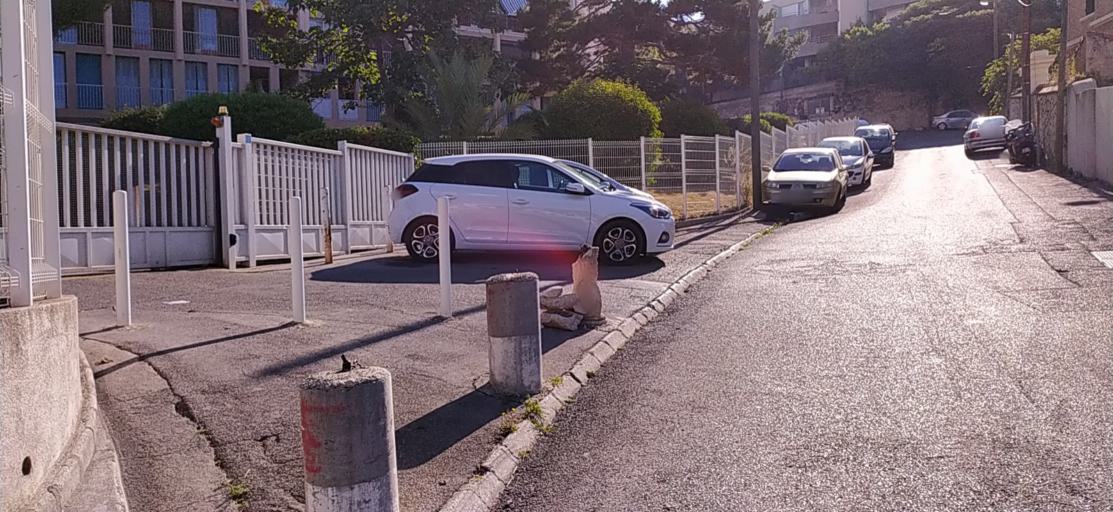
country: FR
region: Provence-Alpes-Cote d'Azur
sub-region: Departement des Bouches-du-Rhone
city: Marseille 14
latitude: 43.3378
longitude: 5.3536
